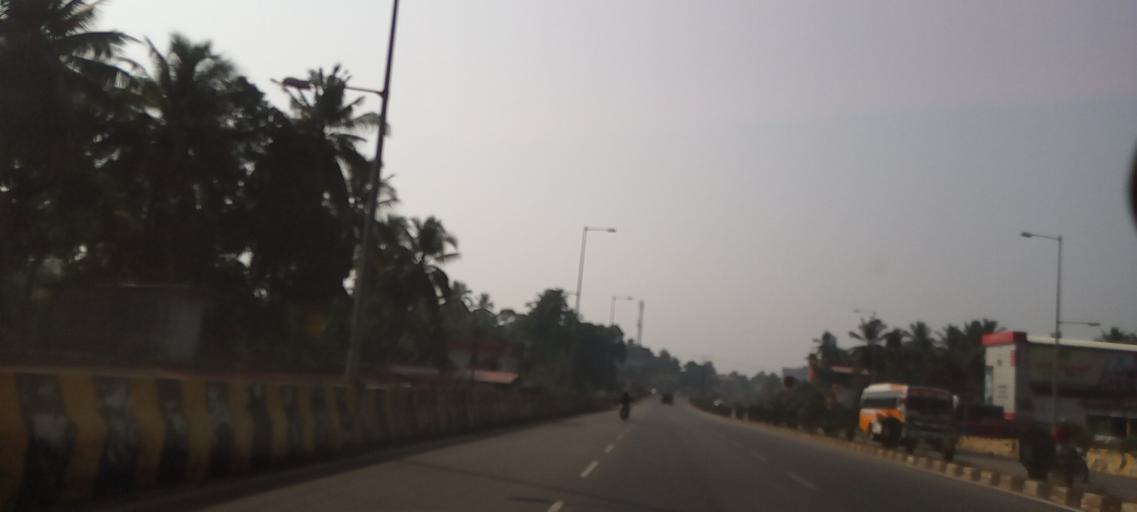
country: IN
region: Karnataka
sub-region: Udupi
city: Coondapoor
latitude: 13.5274
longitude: 74.7053
